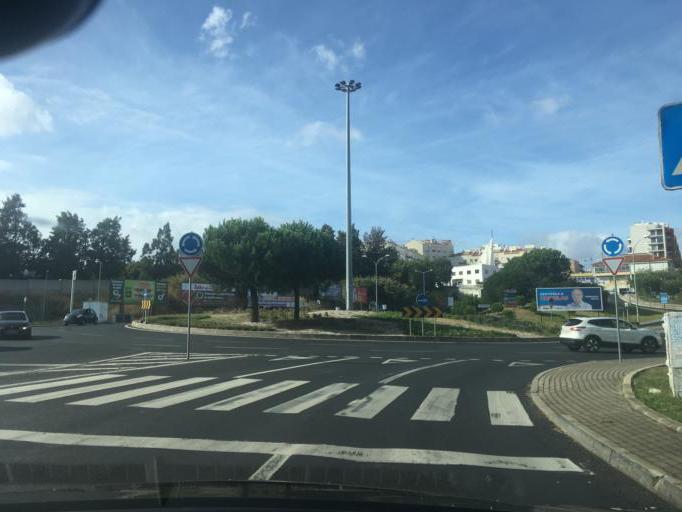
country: PT
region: Lisbon
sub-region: Odivelas
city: Odivelas
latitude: 38.7839
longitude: -9.1915
